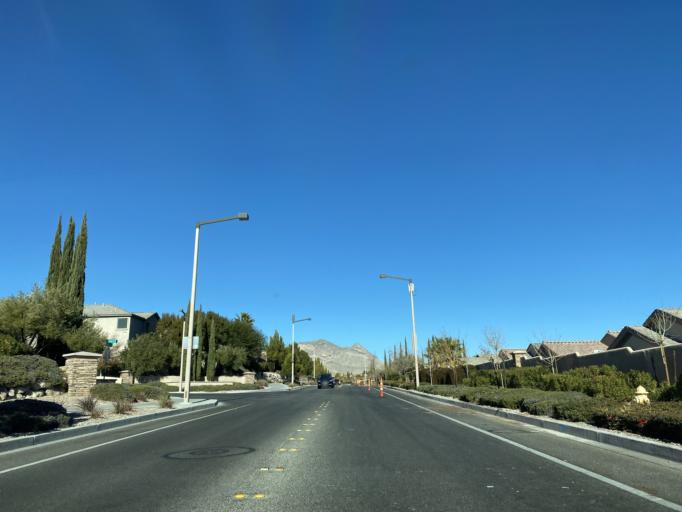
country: US
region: Nevada
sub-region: Clark County
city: Summerlin South
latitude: 36.1660
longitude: -115.3498
